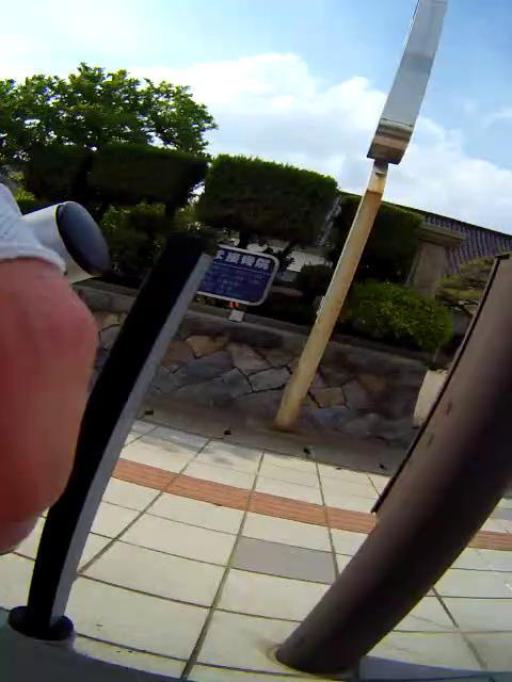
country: JP
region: Toyama
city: Takaoka
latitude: 36.7452
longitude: 137.0108
